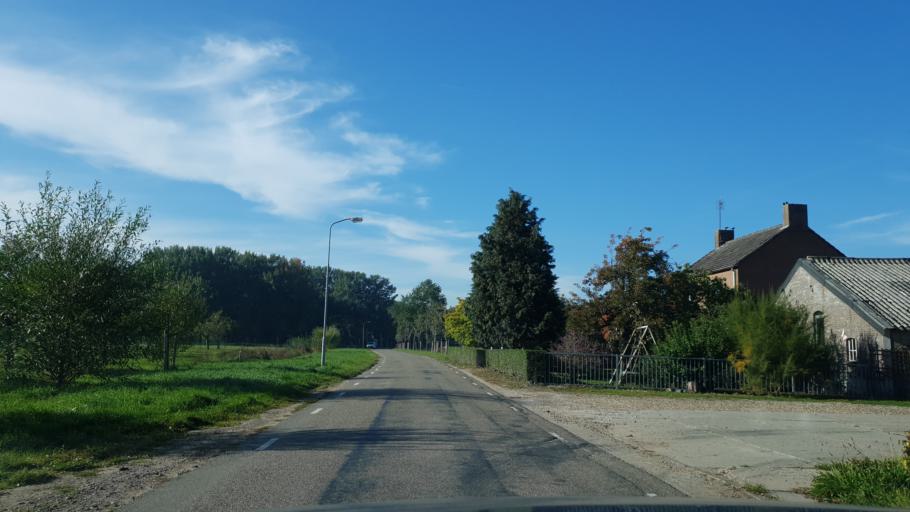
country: NL
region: Gelderland
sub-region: Gemeente Beuningen
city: Beuningen
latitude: 51.8563
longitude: 5.7891
